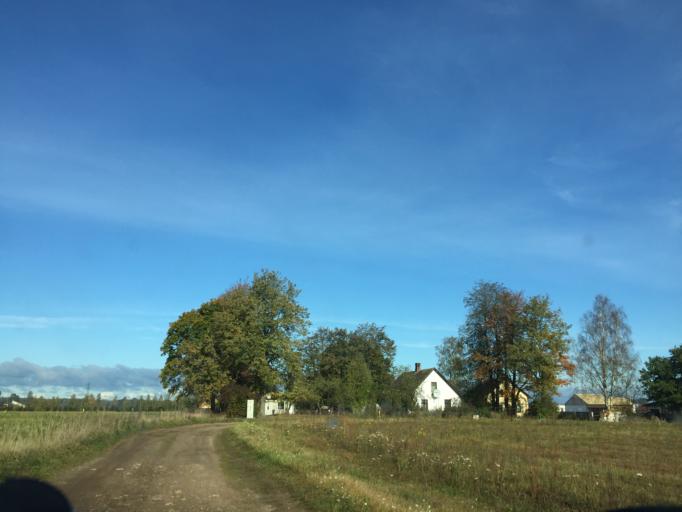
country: LV
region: Adazi
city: Adazi
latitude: 57.0888
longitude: 24.3061
